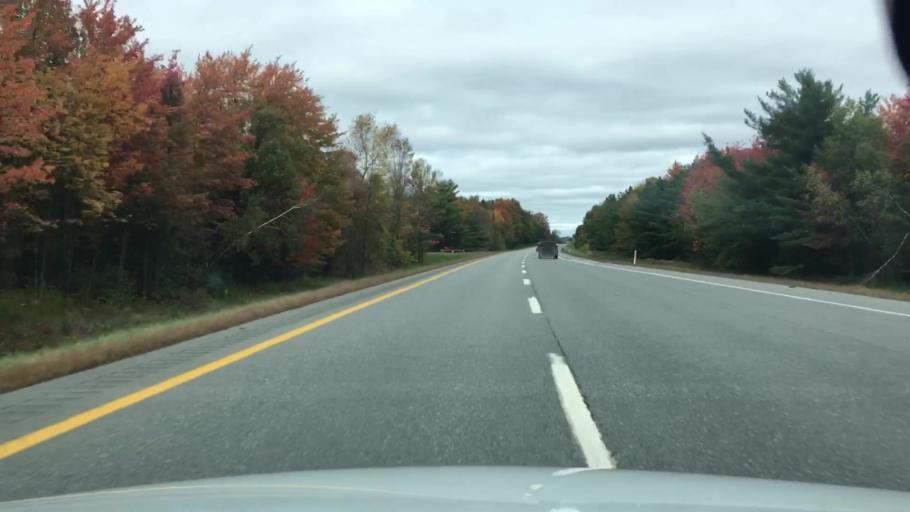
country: US
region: Maine
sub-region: Kennebec County
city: Clinton
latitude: 44.6437
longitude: -69.5233
